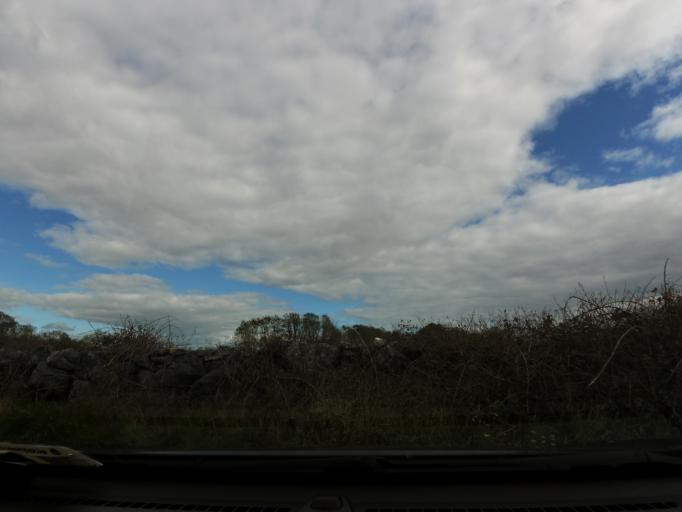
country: IE
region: Connaught
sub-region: County Galway
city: Moycullen
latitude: 53.3582
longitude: -9.1558
